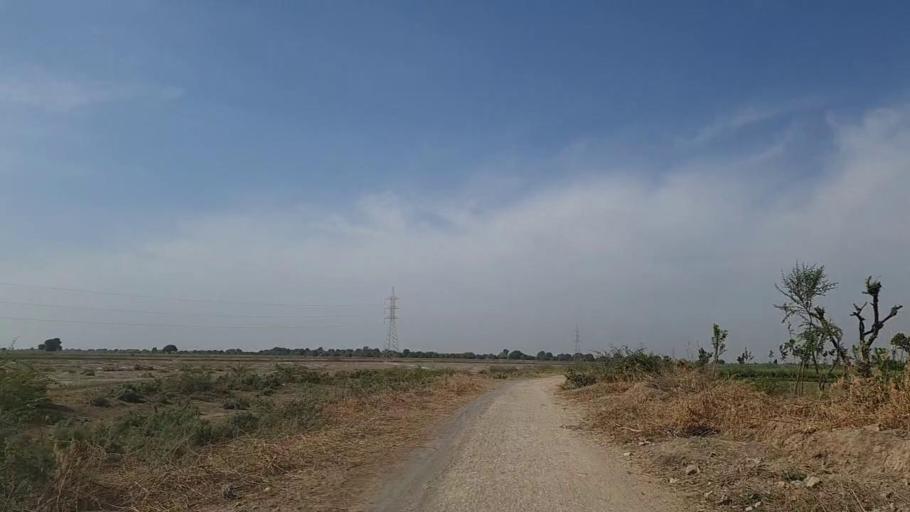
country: PK
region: Sindh
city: Samaro
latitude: 25.2100
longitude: 69.4560
